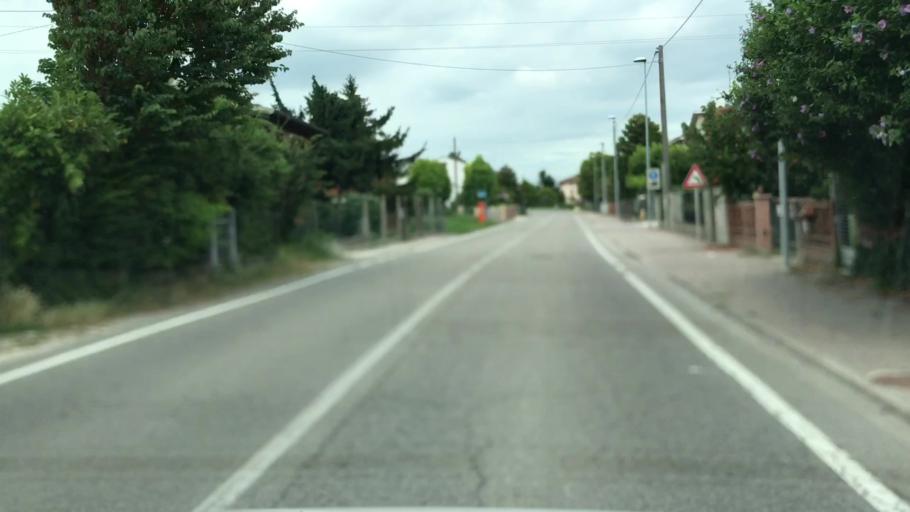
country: IT
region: Lombardy
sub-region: Provincia di Mantova
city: Quistello
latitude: 45.0315
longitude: 11.0066
